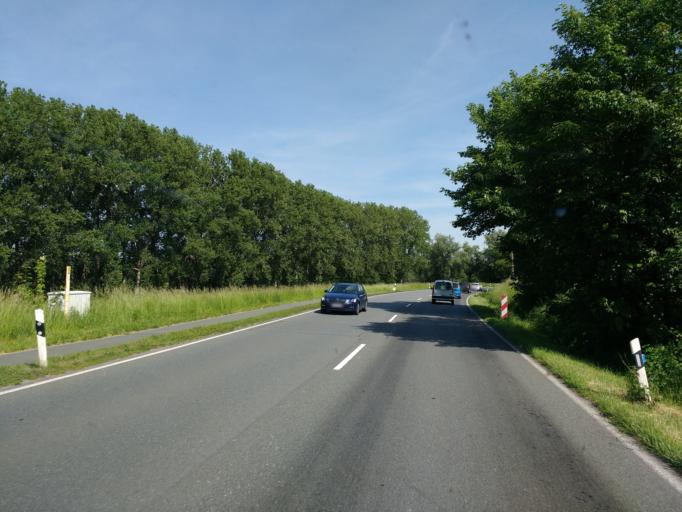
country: DE
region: North Rhine-Westphalia
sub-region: Regierungsbezirk Detmold
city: Bad Salzuflen
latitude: 52.0852
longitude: 8.7117
